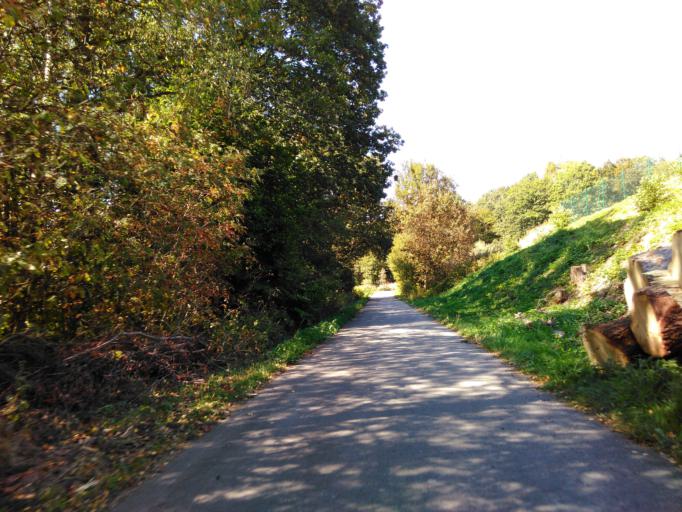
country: LU
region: Diekirch
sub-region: Canton de Redange
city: Rambrouch
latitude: 49.8391
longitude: 5.8132
